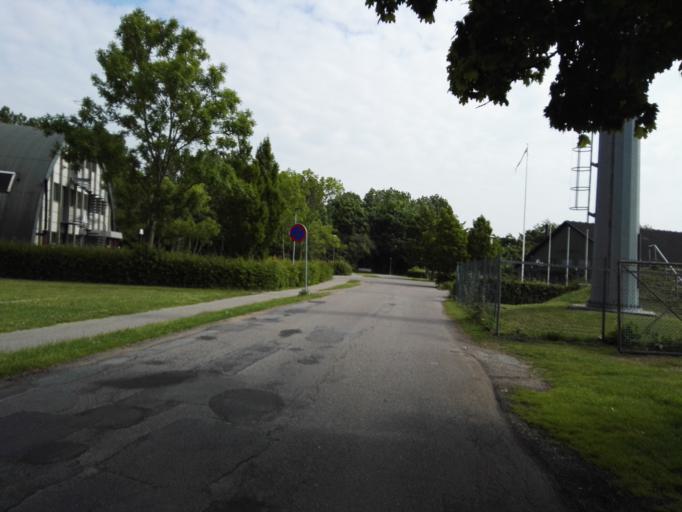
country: DK
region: Capital Region
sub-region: Egedal Kommune
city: Olstykke
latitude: 55.7833
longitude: 12.1448
